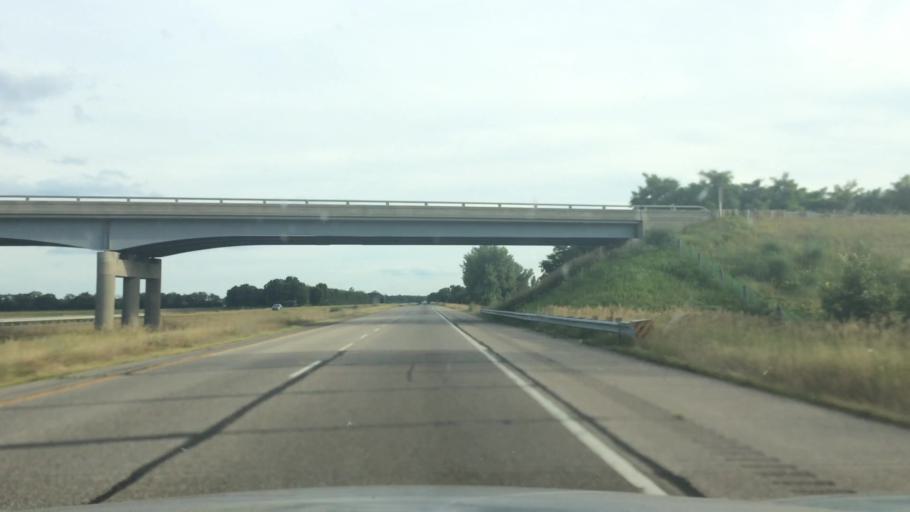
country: US
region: Wisconsin
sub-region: Waushara County
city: Wautoma
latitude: 44.1854
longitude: -89.5268
